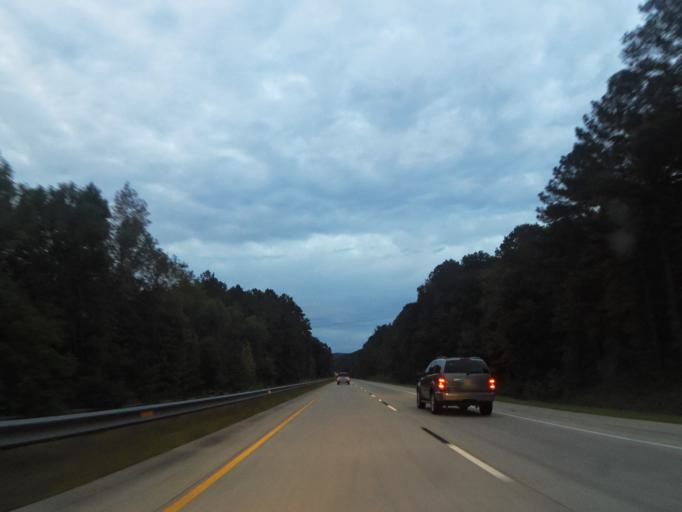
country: US
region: Alabama
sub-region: Etowah County
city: Gadsden
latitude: 34.0996
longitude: -86.0031
